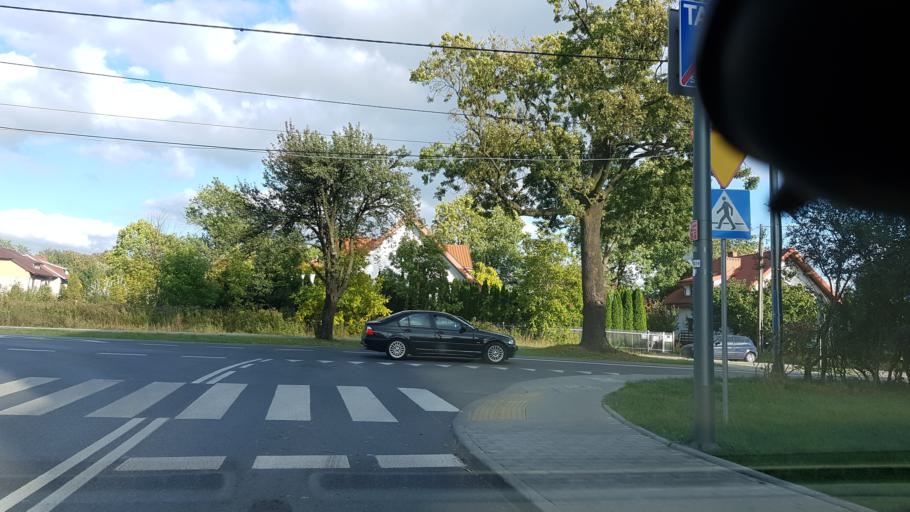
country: PL
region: Masovian Voivodeship
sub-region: Warszawa
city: Targowek
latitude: 52.3125
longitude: 21.0295
